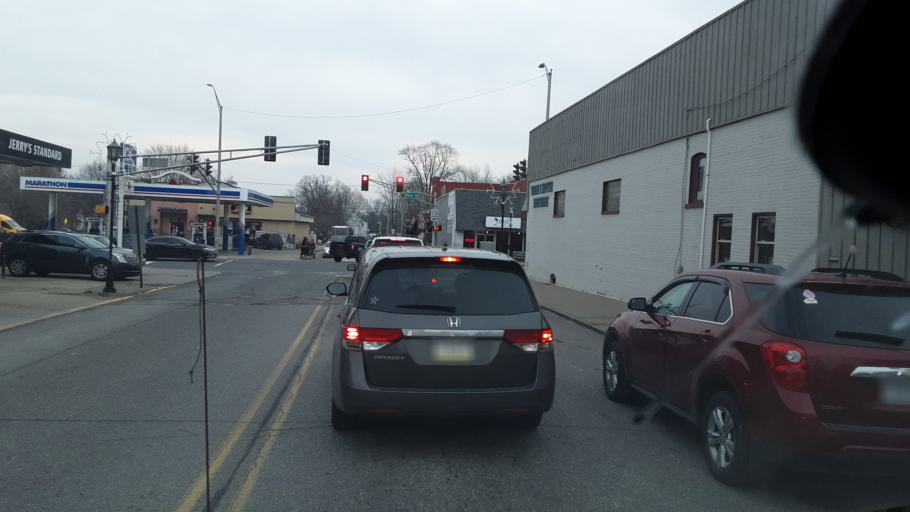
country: US
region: Indiana
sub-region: Elkhart County
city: Middlebury
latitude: 41.6752
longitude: -85.7066
